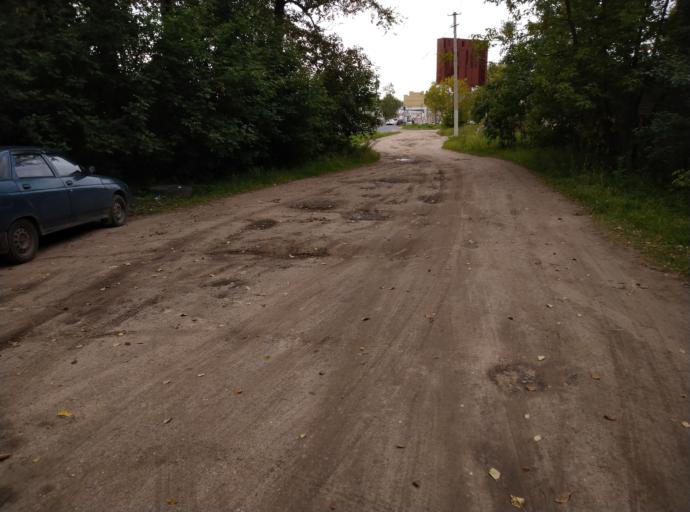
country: RU
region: Kostroma
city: Oktyabr'skiy
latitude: 57.7799
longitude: 40.9716
